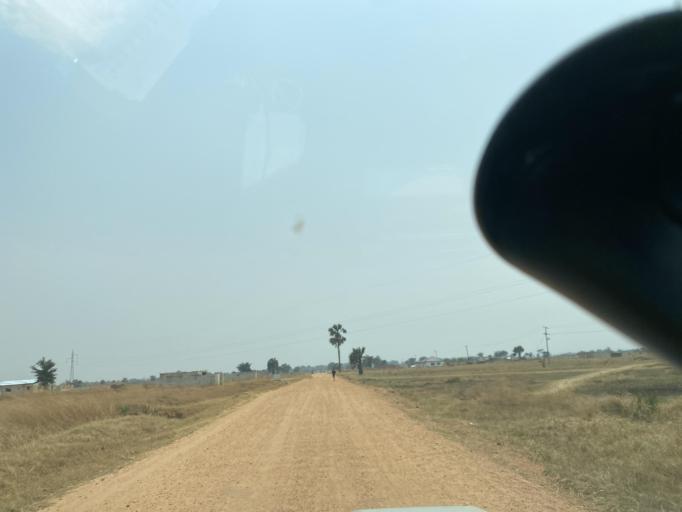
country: ZM
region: Lusaka
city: Kafue
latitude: -15.6391
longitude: 28.0983
